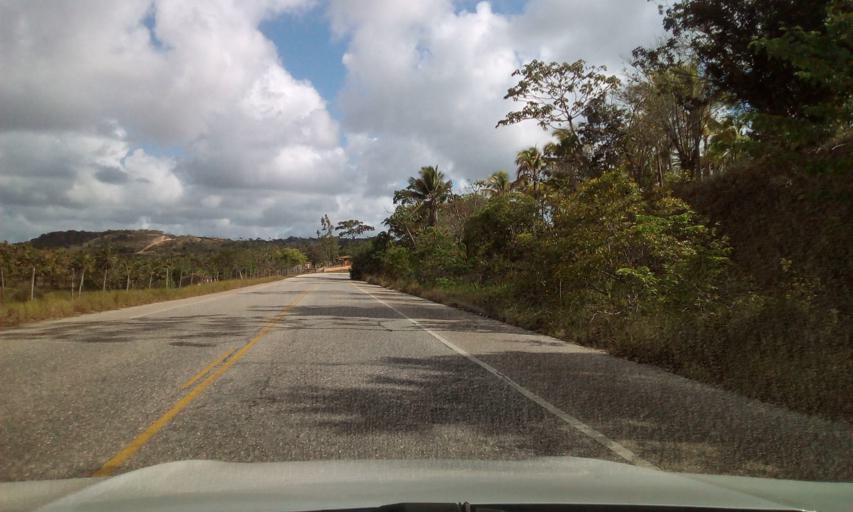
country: BR
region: Sergipe
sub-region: Indiaroba
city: Indiaroba
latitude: -11.4463
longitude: -37.4956
